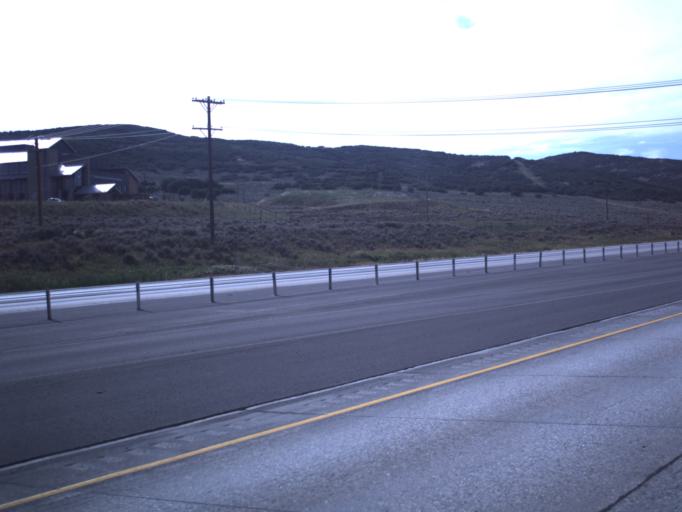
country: US
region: Utah
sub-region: Summit County
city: Park City
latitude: 40.6886
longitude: -111.4655
